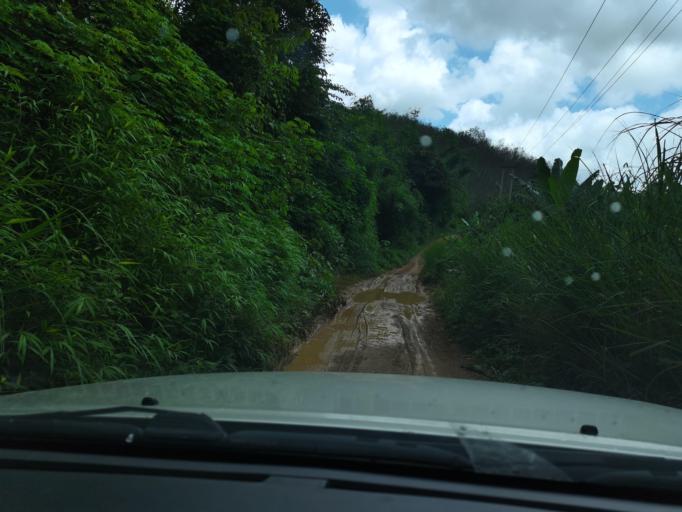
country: LA
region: Loungnamtha
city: Muang Long
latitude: 20.7539
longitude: 101.0178
